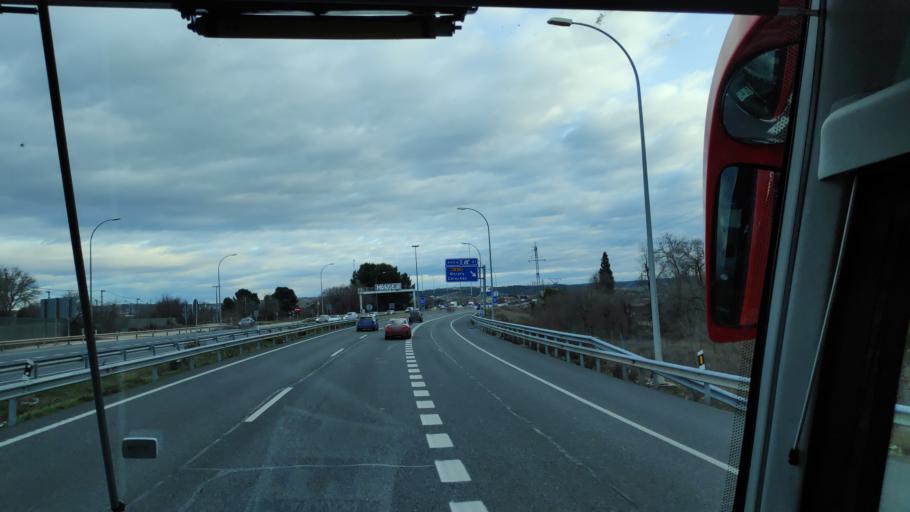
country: ES
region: Madrid
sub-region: Provincia de Madrid
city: Vaciamadrid
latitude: 40.3234
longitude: -3.5170
